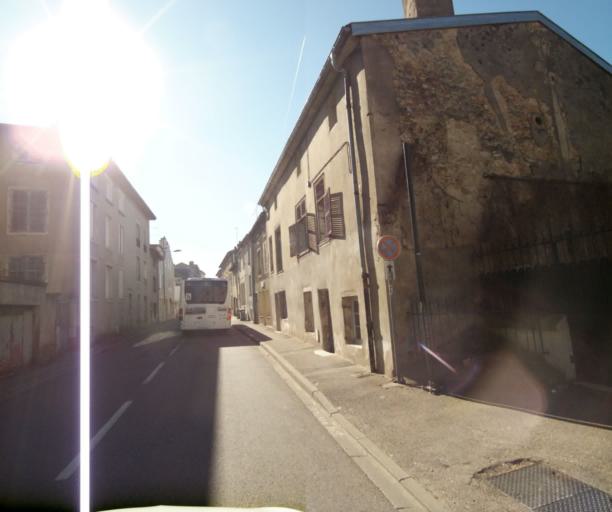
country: FR
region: Lorraine
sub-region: Departement de Meurthe-et-Moselle
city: Malzeville
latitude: 48.7096
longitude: 6.1846
